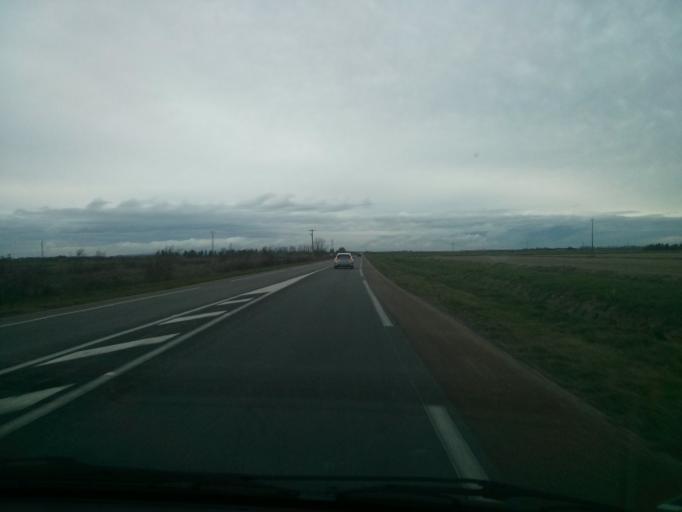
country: FR
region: Languedoc-Roussillon
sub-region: Departement du Gard
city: Bellegarde
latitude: 43.6800
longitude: 4.5119
